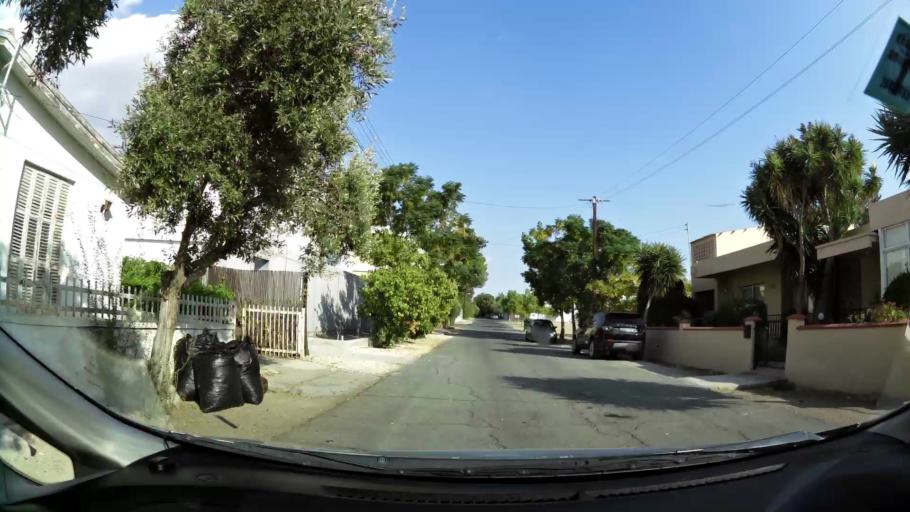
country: CY
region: Lefkosia
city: Nicosia
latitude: 35.1782
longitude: 33.3409
